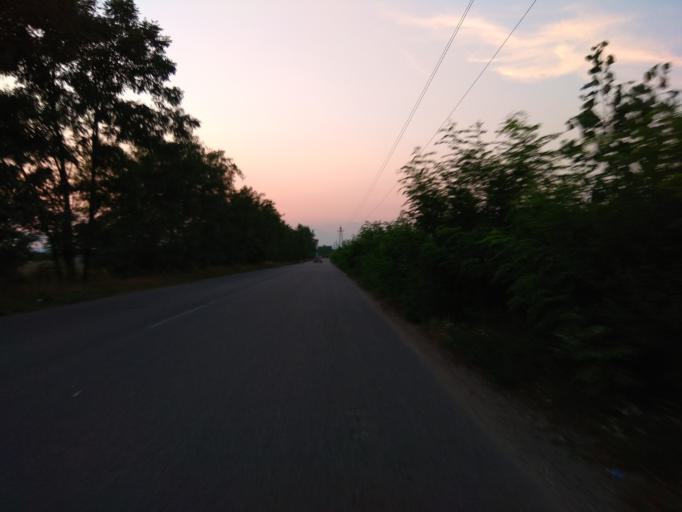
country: HU
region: Borsod-Abauj-Zemplen
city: Emod
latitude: 47.9105
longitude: 20.8530
